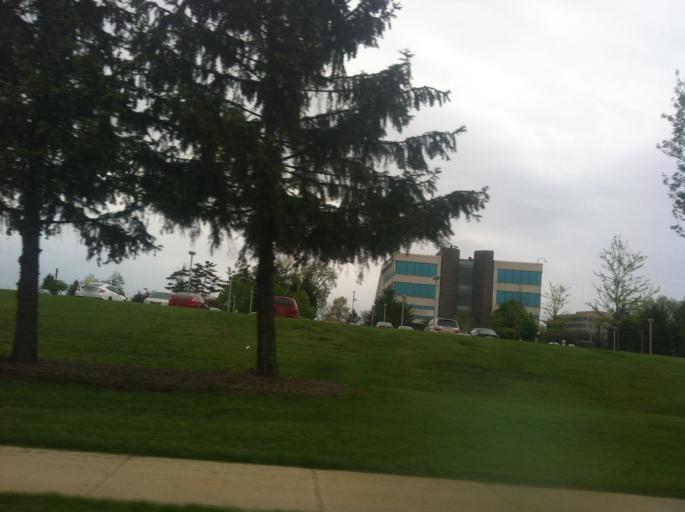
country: US
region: Illinois
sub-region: DuPage County
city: Lisle
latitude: 41.8044
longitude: -88.0505
